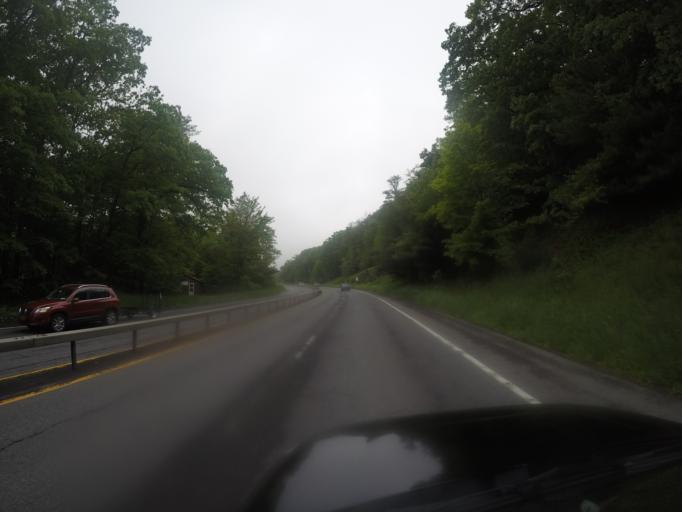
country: US
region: New York
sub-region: Ulster County
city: West Hurley
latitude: 41.9718
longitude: -74.0752
